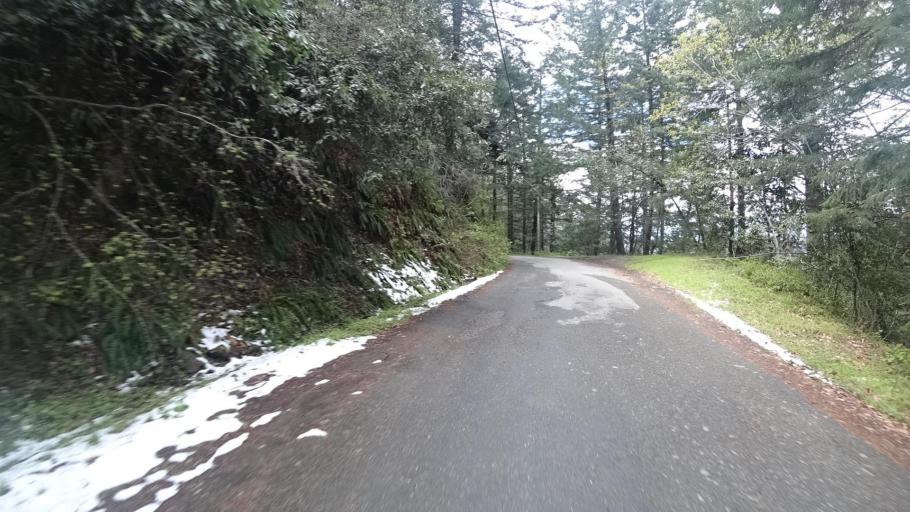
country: US
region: California
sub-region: Humboldt County
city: Blue Lake
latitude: 40.8762
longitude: -123.8807
